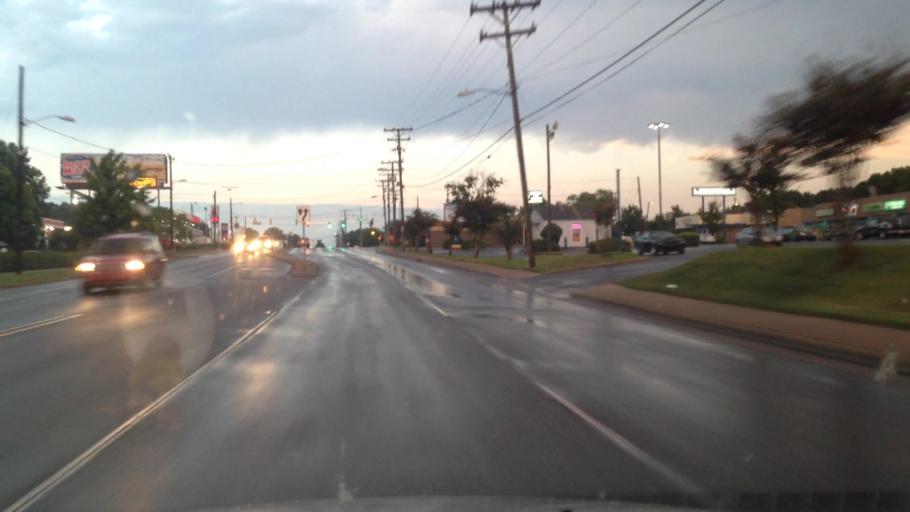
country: US
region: North Carolina
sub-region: Mecklenburg County
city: Pineville
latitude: 35.1508
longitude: -80.8763
